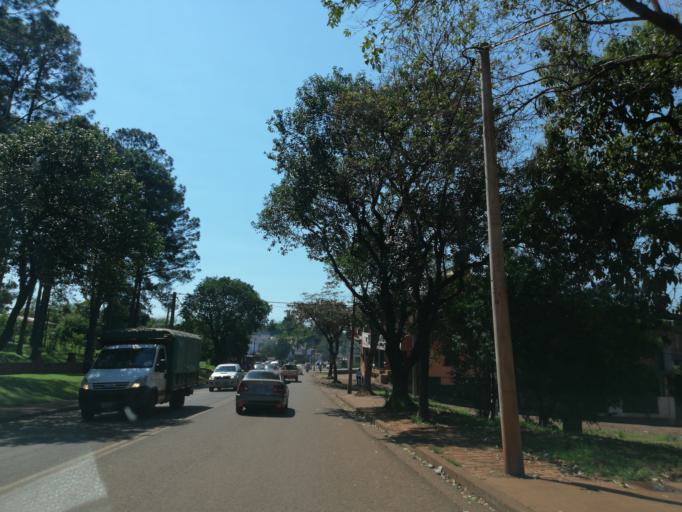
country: AR
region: Misiones
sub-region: Departamento de Eldorado
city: Eldorado
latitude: -26.4041
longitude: -54.6299
